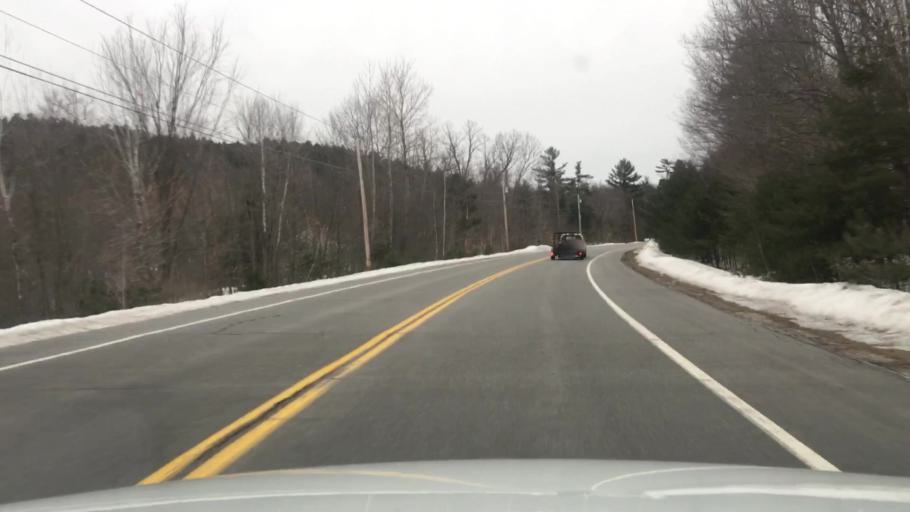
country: US
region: Maine
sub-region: York County
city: Limerick
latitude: 43.7367
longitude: -70.8169
